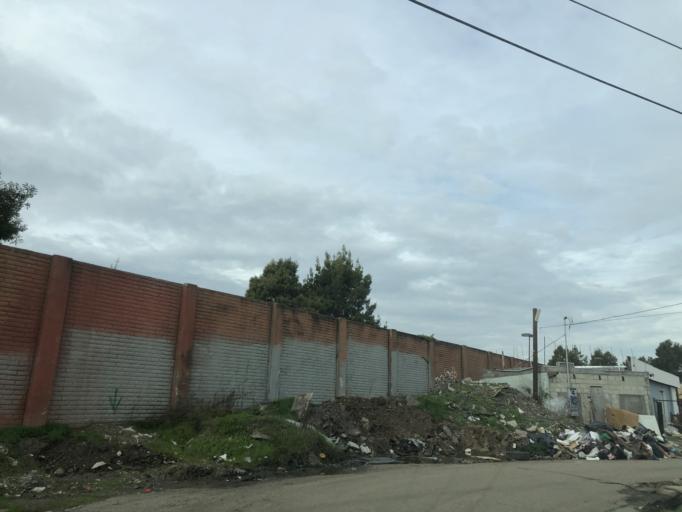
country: US
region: California
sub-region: Alameda County
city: San Leandro
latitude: 37.7393
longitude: -122.1869
